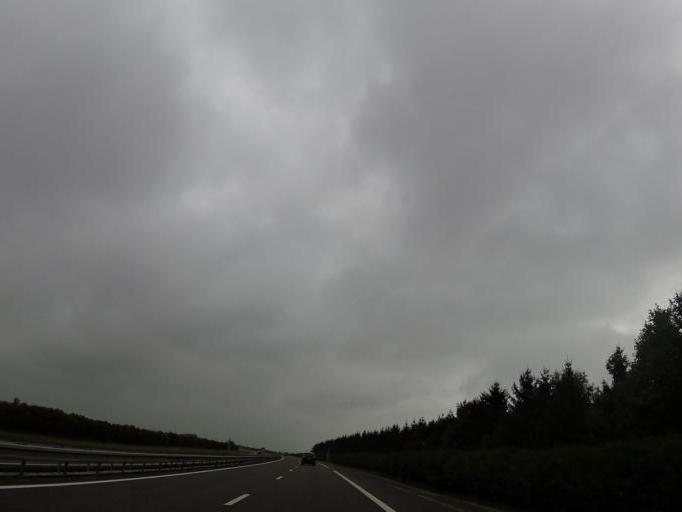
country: FR
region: Champagne-Ardenne
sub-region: Departement de la Marne
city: Chalons-en-Champagne
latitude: 49.0339
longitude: 4.3618
